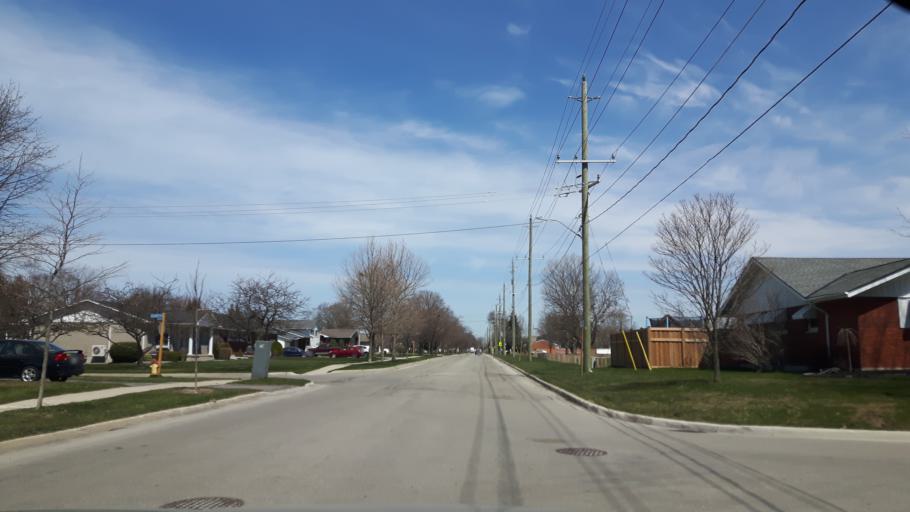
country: CA
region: Ontario
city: Goderich
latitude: 43.7311
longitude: -81.7163
